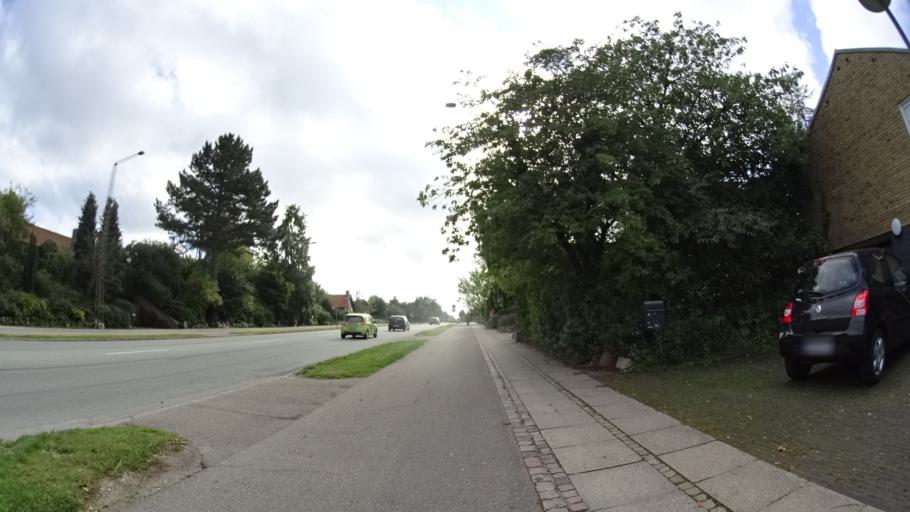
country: DK
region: Central Jutland
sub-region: Arhus Kommune
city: Arhus
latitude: 56.1317
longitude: 10.1888
